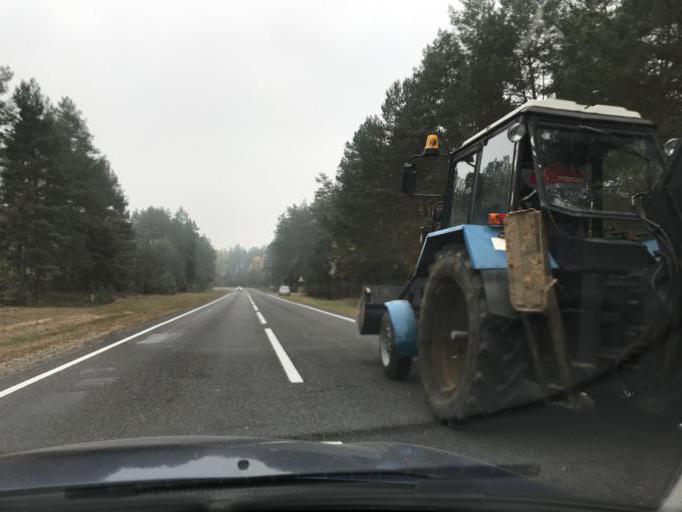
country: BY
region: Grodnenskaya
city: Hrodna
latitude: 53.8507
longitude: 23.8910
